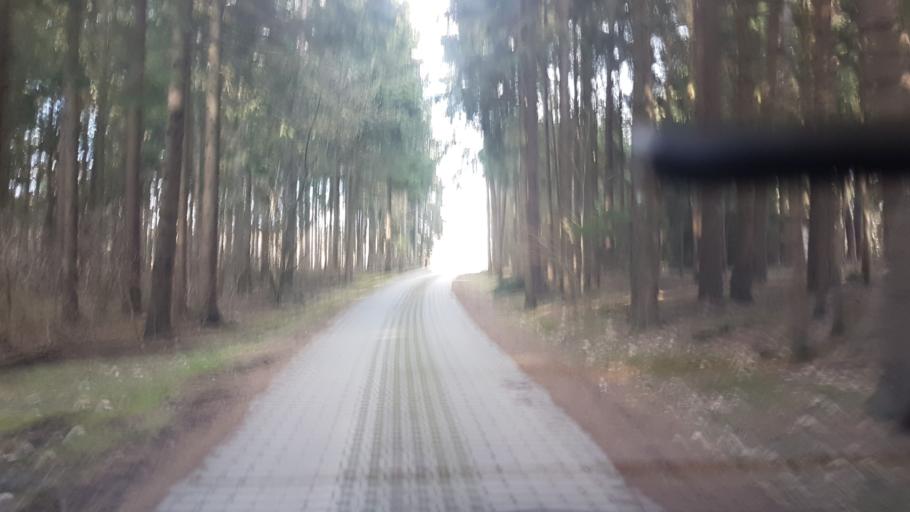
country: DE
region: Bavaria
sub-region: Upper Franconia
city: Stadelhofen
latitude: 50.0002
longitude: 11.2336
